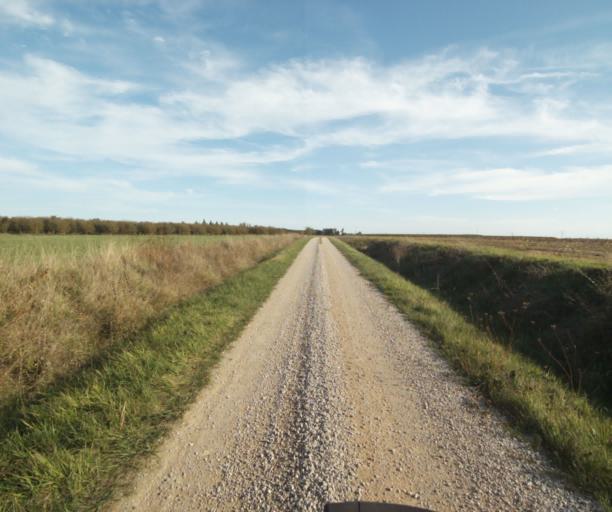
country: FR
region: Midi-Pyrenees
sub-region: Departement du Tarn-et-Garonne
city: Finhan
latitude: 43.9180
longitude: 1.1155
